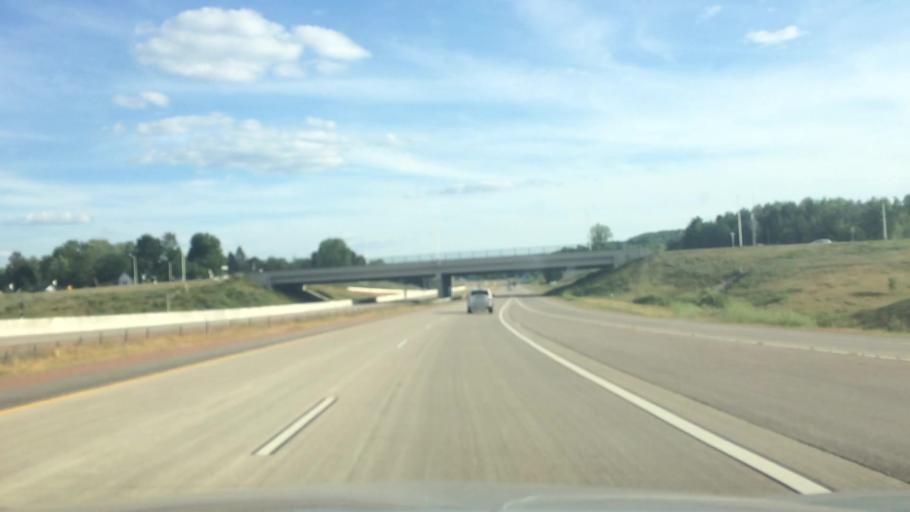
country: US
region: Wisconsin
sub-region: Marathon County
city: Wausau
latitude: 44.9880
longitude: -89.6567
